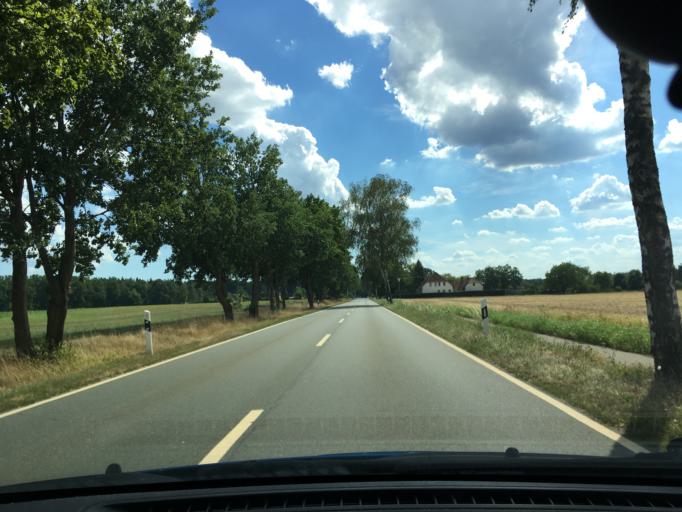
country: DE
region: Lower Saxony
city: Wriedel
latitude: 52.9993
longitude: 10.2604
